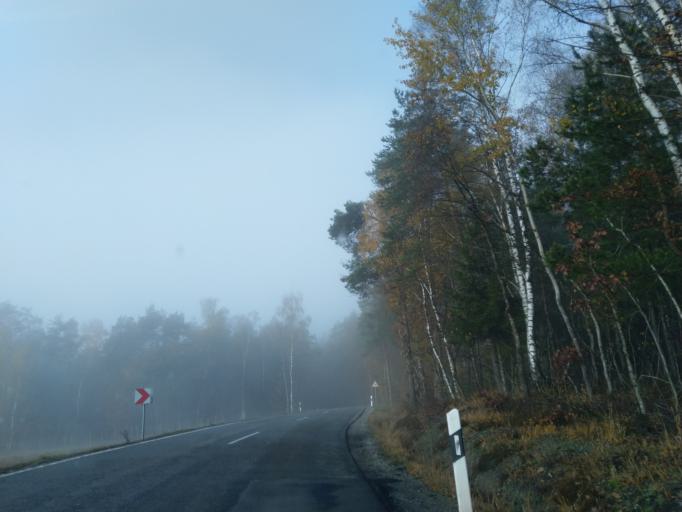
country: DE
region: Bavaria
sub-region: Lower Bavaria
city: Aussernzell
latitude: 48.7298
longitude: 13.1803
